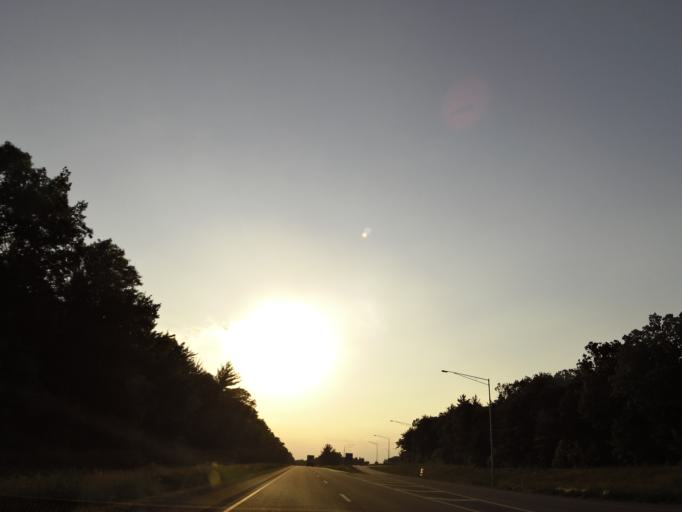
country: US
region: Wisconsin
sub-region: Jackson County
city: Black River Falls
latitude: 44.2441
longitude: -90.7328
